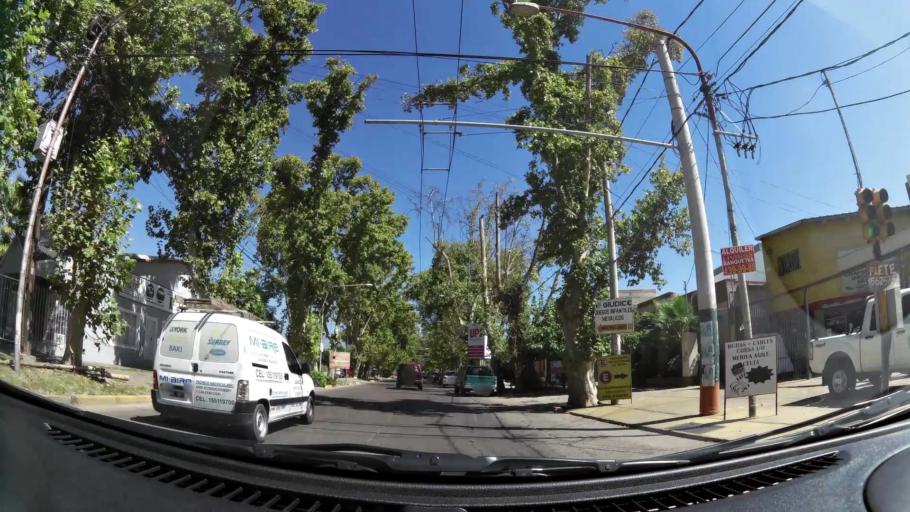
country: AR
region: Mendoza
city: Mendoza
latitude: -32.8946
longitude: -68.8177
